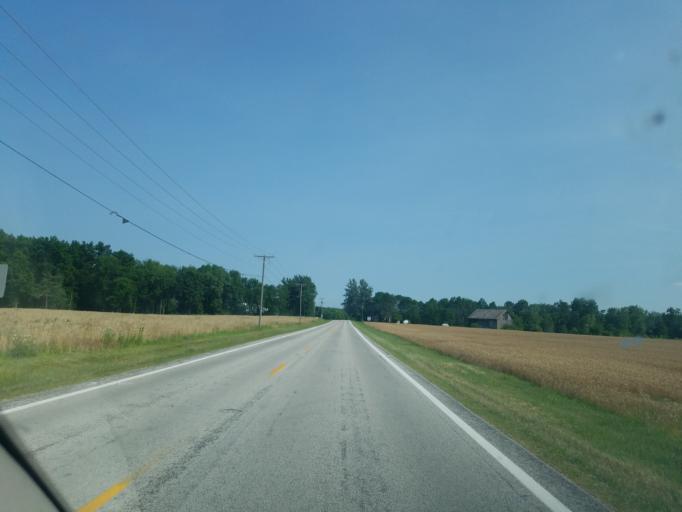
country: US
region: Ohio
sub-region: Wyandot County
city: Carey
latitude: 40.9961
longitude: -83.2689
